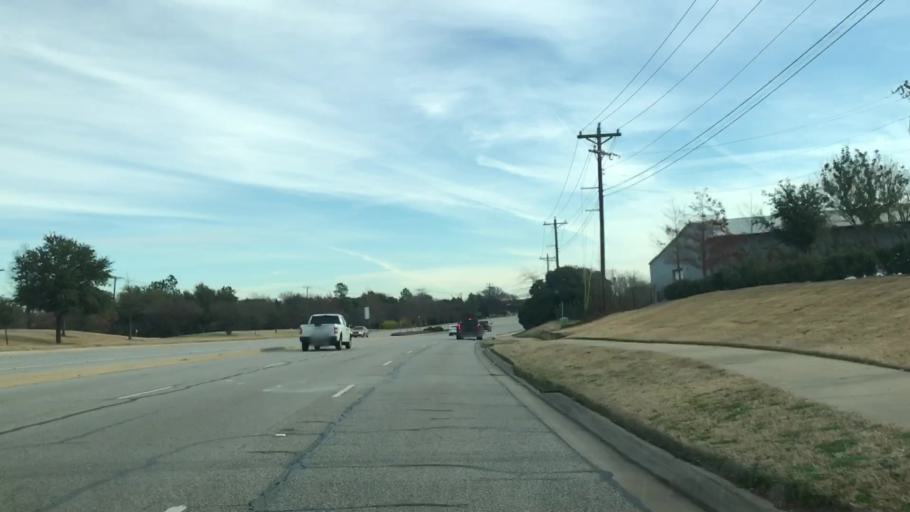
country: US
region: Texas
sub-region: Tarrant County
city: Southlake
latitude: 32.9405
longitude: -97.1809
